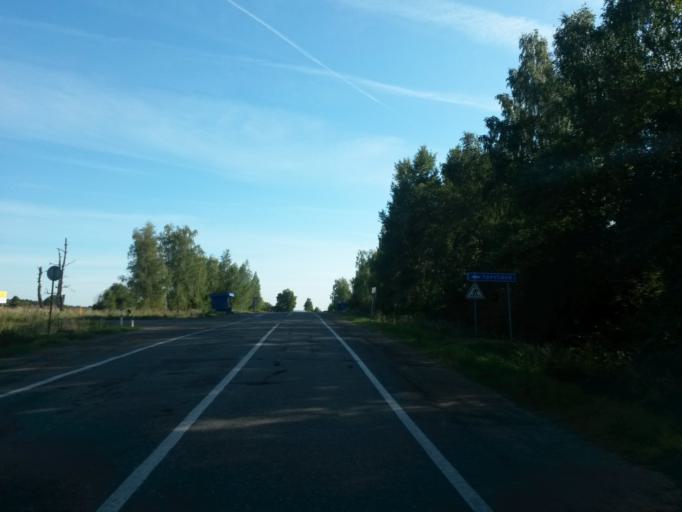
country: RU
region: Jaroslavl
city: Gavrilov-Yam
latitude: 57.3801
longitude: 39.9099
